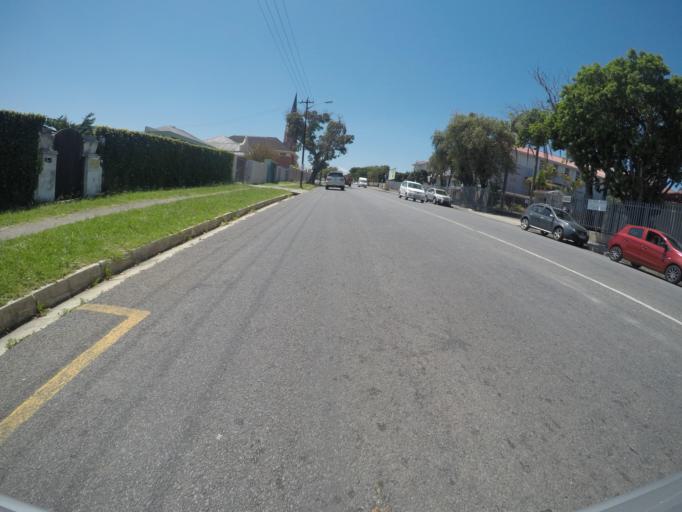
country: ZA
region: Eastern Cape
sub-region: Buffalo City Metropolitan Municipality
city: East London
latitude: -32.9857
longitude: 27.9108
